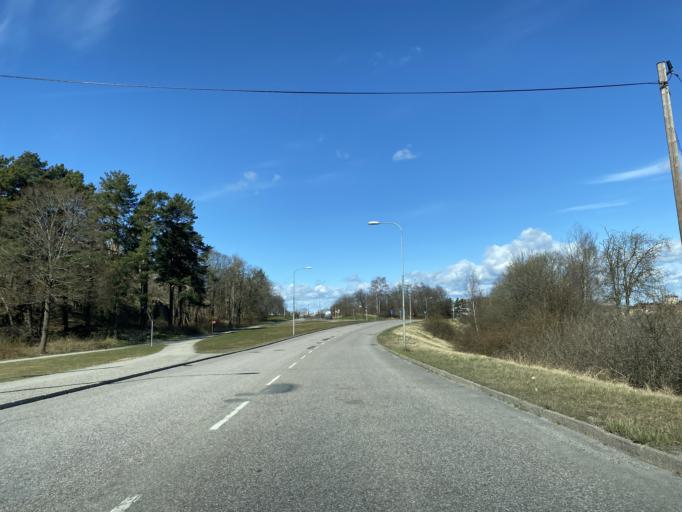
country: SE
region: Stockholm
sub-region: Stockholms Kommun
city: Arsta
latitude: 59.2894
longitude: 18.0381
